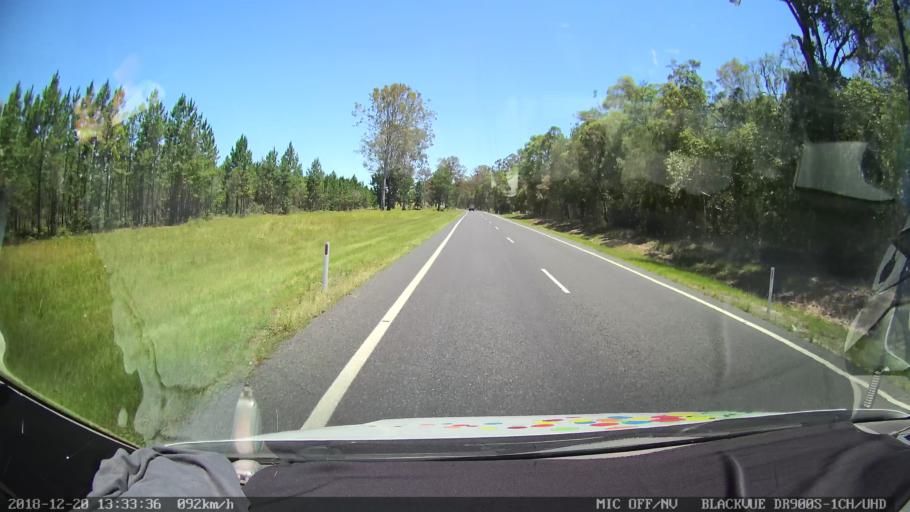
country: AU
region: New South Wales
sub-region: Clarence Valley
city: Gordon
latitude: -29.2476
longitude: 152.9859
